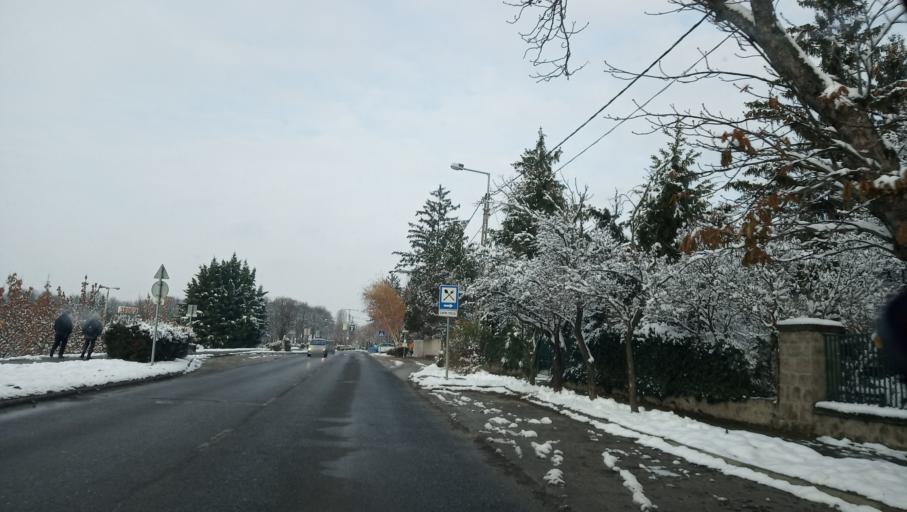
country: HU
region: Komarom-Esztergom
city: Esztergom
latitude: 47.7792
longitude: 18.7517
